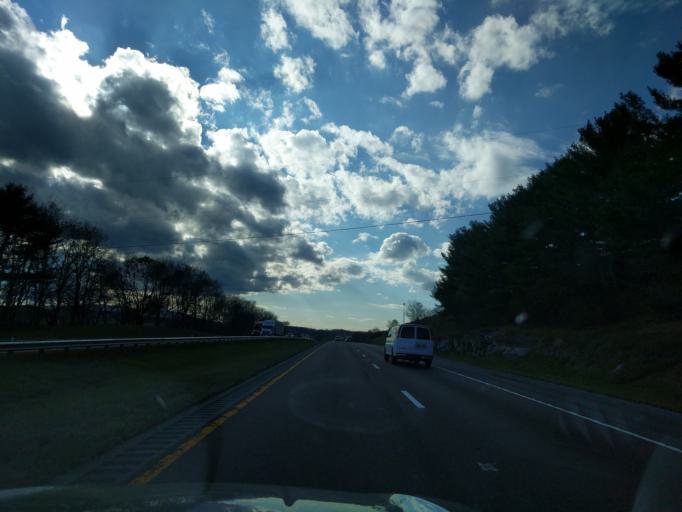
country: US
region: Virginia
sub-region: Wythe County
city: Rural Retreat
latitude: 36.9243
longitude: -81.2164
